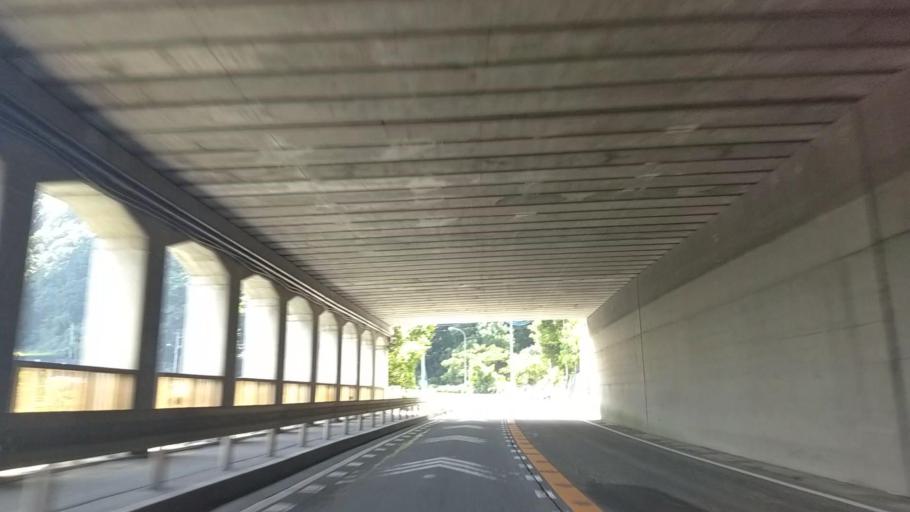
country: JP
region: Yamanashi
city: Ryuo
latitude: 35.5049
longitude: 138.4473
